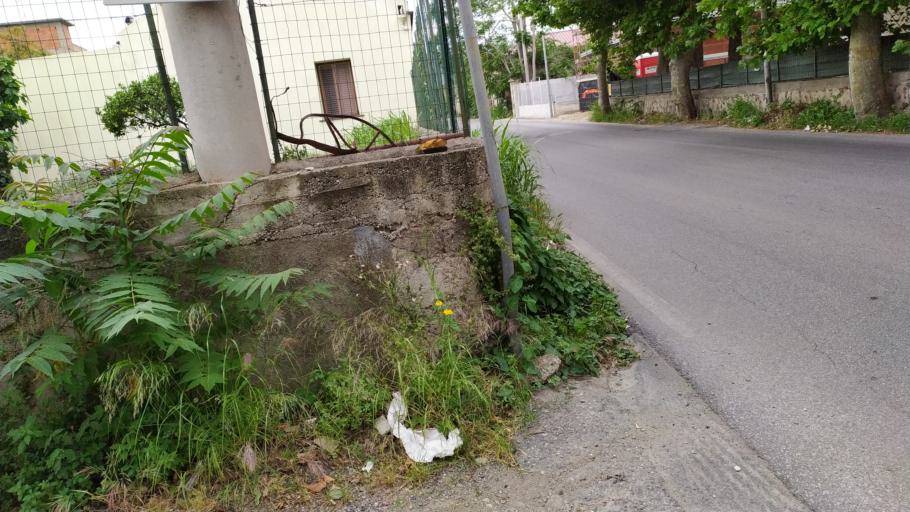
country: IT
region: Sicily
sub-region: Messina
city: Meri
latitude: 38.1861
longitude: 15.2539
